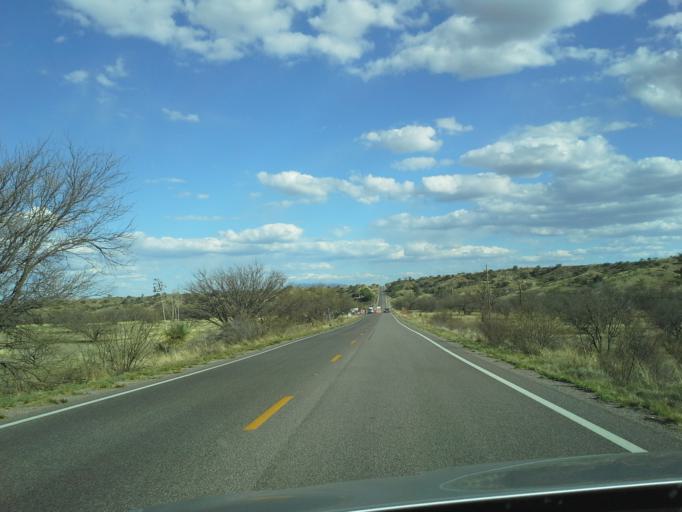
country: US
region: Arizona
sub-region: Pima County
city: Corona de Tucson
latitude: 31.7836
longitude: -110.6947
